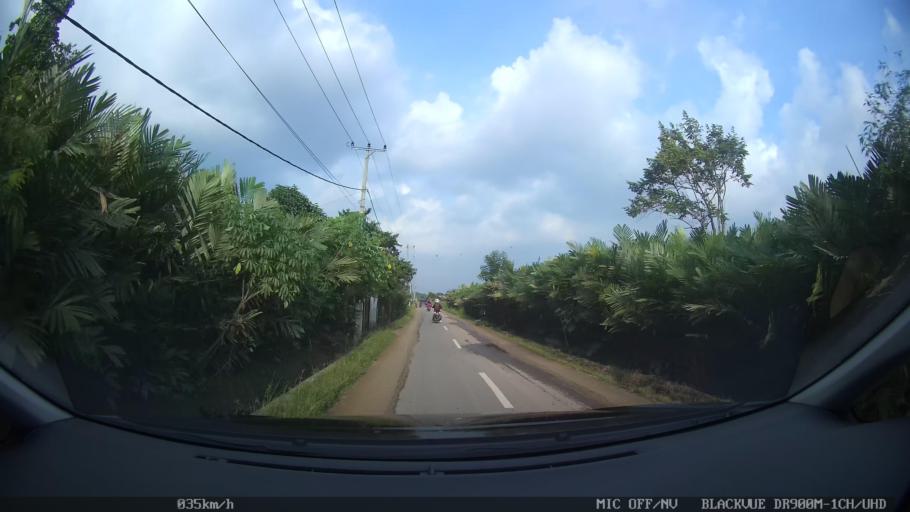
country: ID
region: Lampung
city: Kedaton
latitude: -5.3920
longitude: 105.3328
